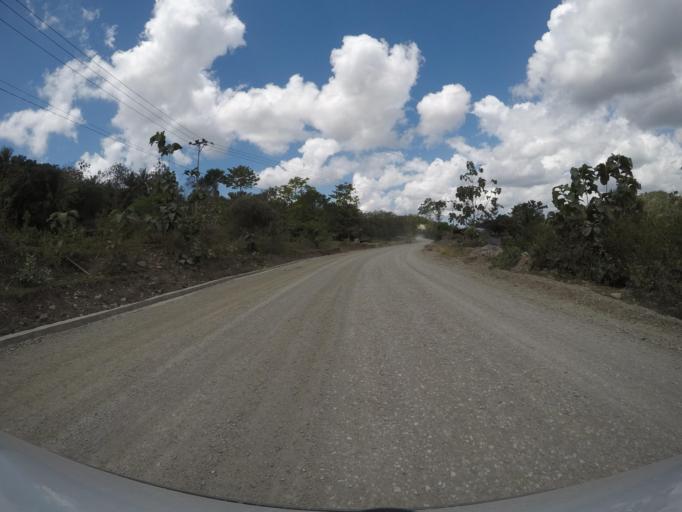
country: TL
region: Viqueque
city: Viqueque
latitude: -8.8212
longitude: 126.3786
